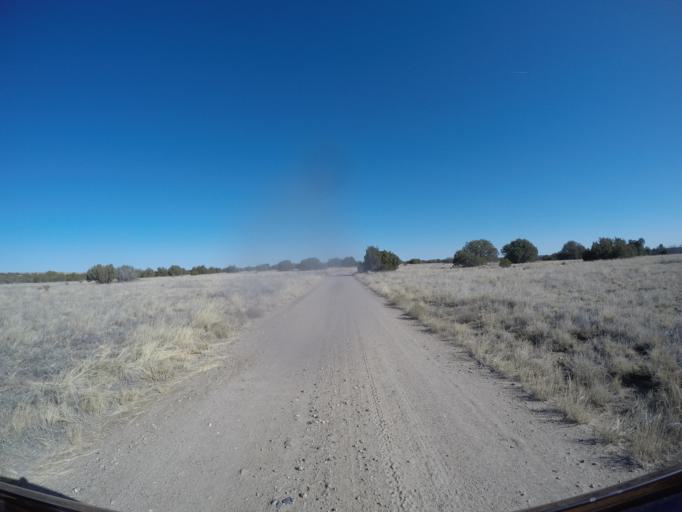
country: US
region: Colorado
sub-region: Otero County
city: La Junta
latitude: 37.6578
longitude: -103.5859
